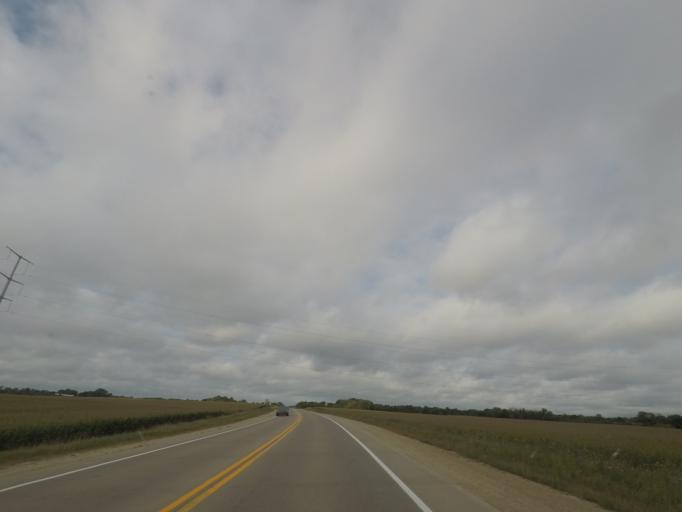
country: US
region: Wisconsin
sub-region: Jefferson County
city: Cambridge
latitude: 43.0191
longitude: -89.0405
